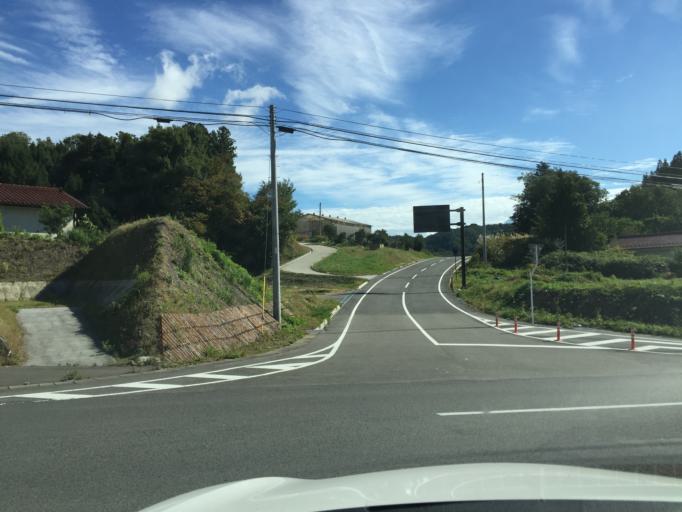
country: JP
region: Fukushima
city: Funehikimachi-funehiki
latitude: 37.4228
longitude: 140.5492
